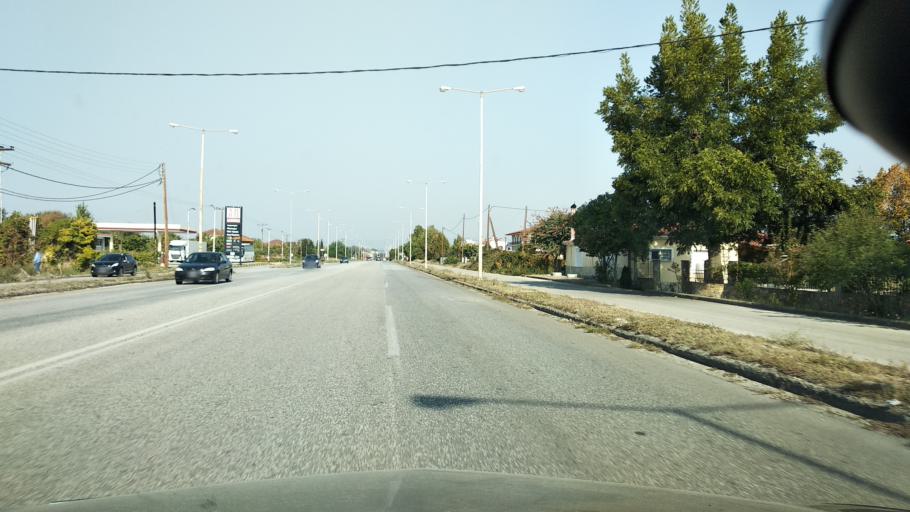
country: GR
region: Thessaly
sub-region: Trikala
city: Pyrgetos
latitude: 39.5799
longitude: 21.7423
